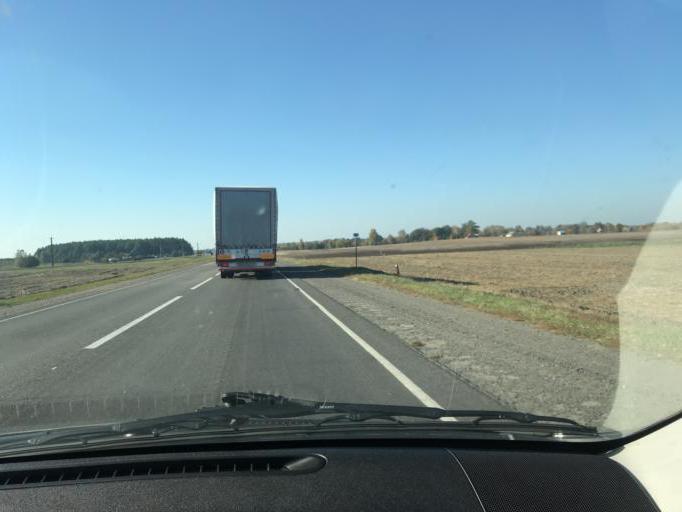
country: BY
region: Brest
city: Davyd-Haradok
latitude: 52.2413
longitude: 27.1973
